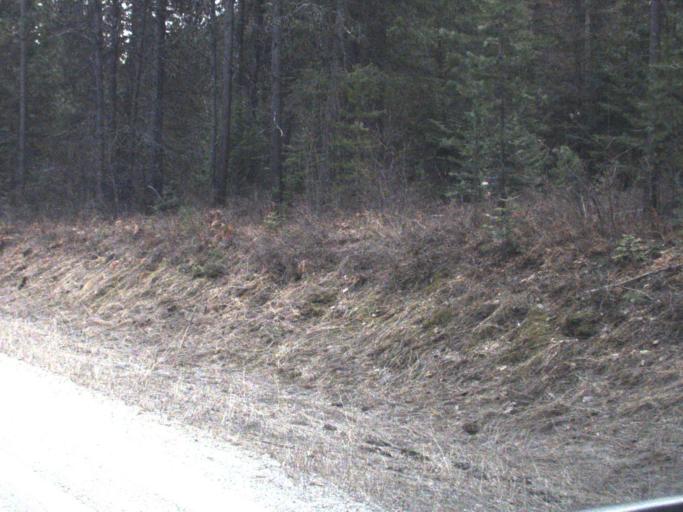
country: US
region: Washington
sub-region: Pend Oreille County
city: Newport
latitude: 48.5453
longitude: -117.3149
